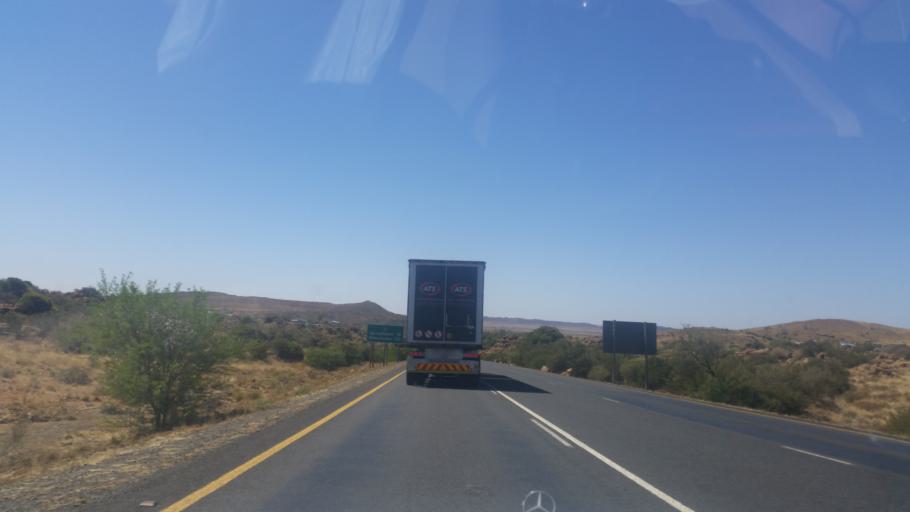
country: ZA
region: Northern Cape
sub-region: Pixley ka Seme District Municipality
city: Colesberg
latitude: -30.7181
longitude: 25.0943
